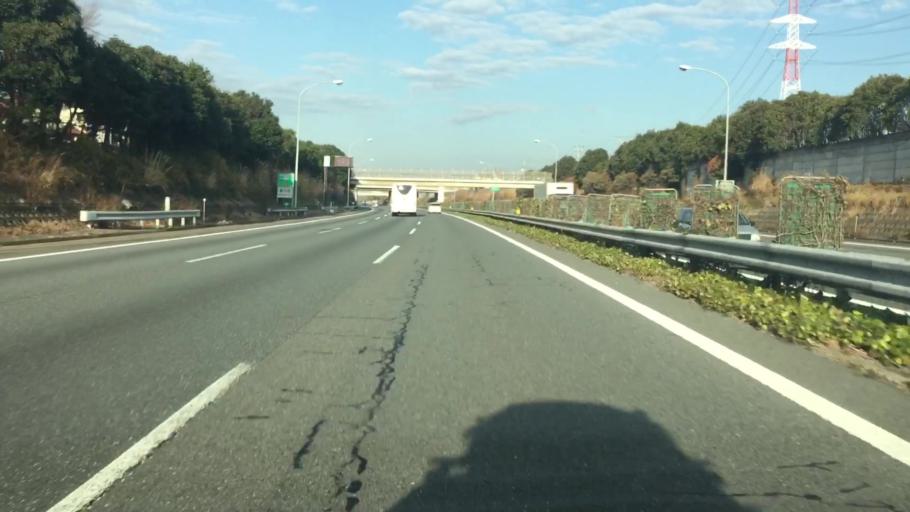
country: JP
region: Saitama
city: Sakado
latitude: 36.0387
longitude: 139.3739
